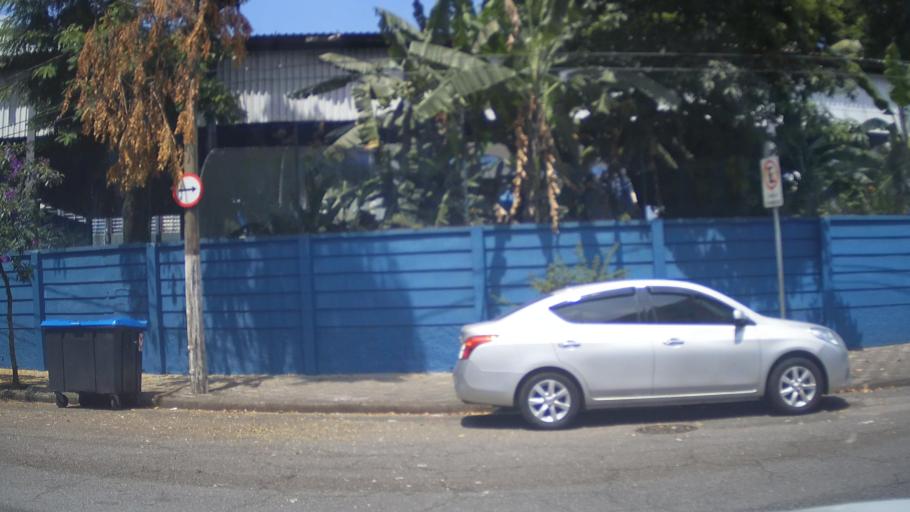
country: BR
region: Sao Paulo
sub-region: Santos
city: Santos
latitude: -23.9795
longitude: -46.2998
